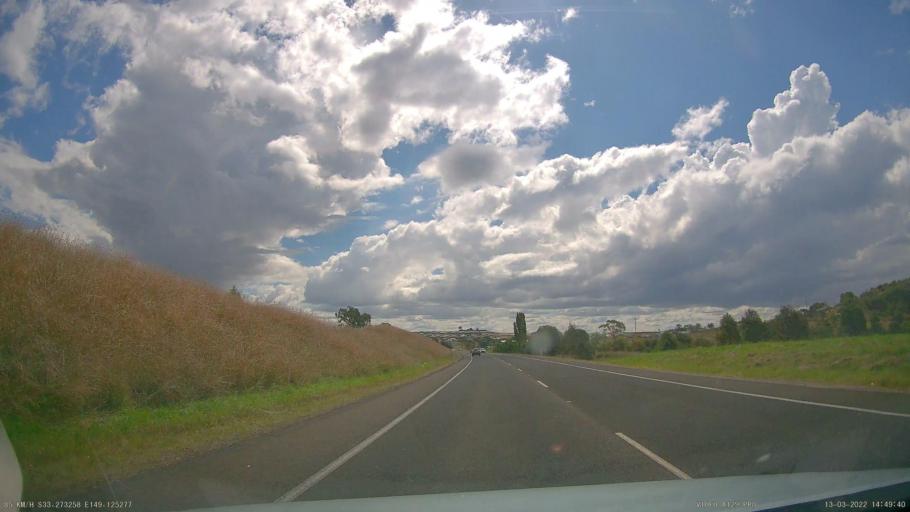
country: AU
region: New South Wales
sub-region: Orange Municipality
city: Orange
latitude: -33.2731
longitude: 149.1250
